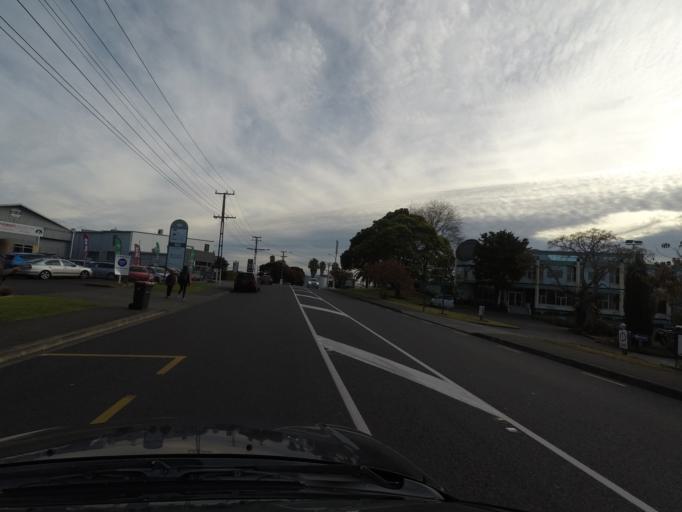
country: NZ
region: Auckland
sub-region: Auckland
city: Tamaki
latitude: -36.8924
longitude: 174.8292
